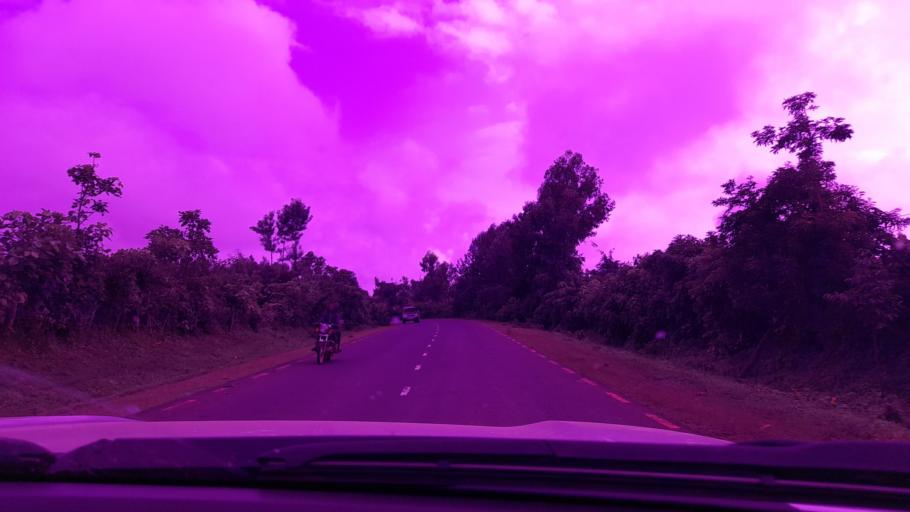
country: ET
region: Oromiya
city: Bedele
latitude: 8.3017
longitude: 36.4490
